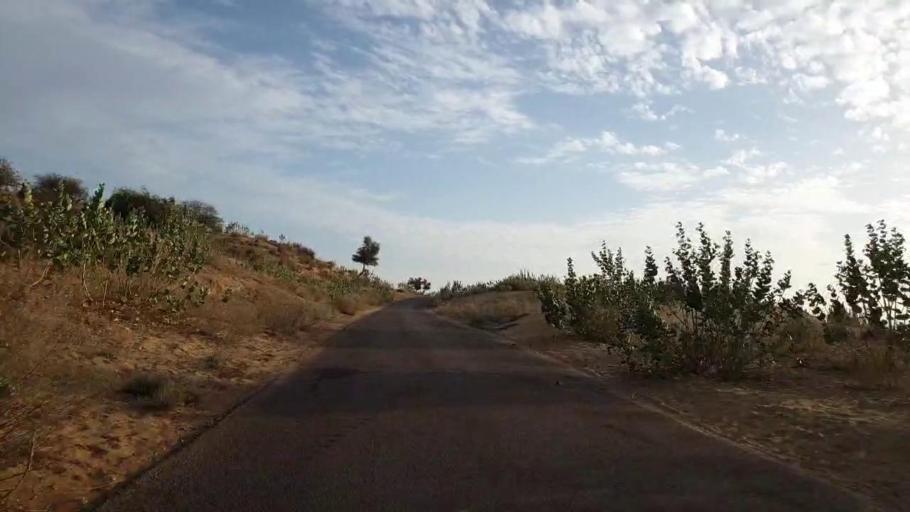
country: PK
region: Sindh
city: Umarkot
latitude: 25.1292
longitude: 70.0079
